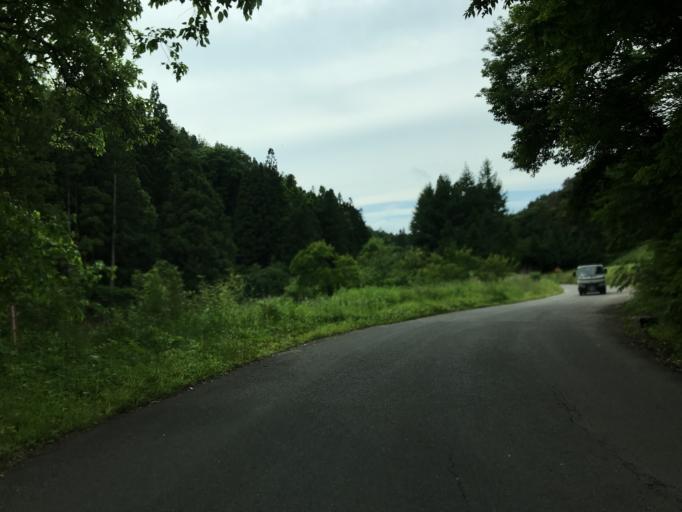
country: JP
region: Fukushima
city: Funehikimachi-funehiki
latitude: 37.4363
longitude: 140.7860
